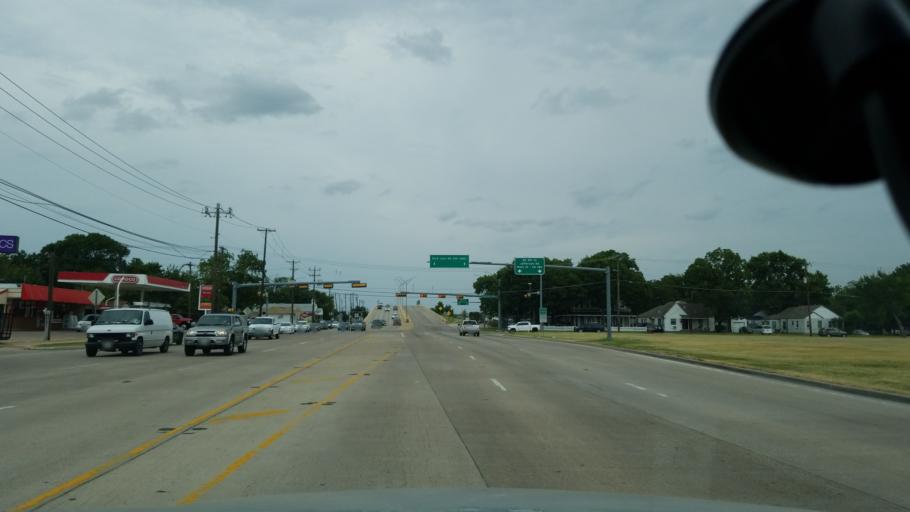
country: US
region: Texas
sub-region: Dallas County
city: Grand Prairie
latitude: 32.7413
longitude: -96.9946
